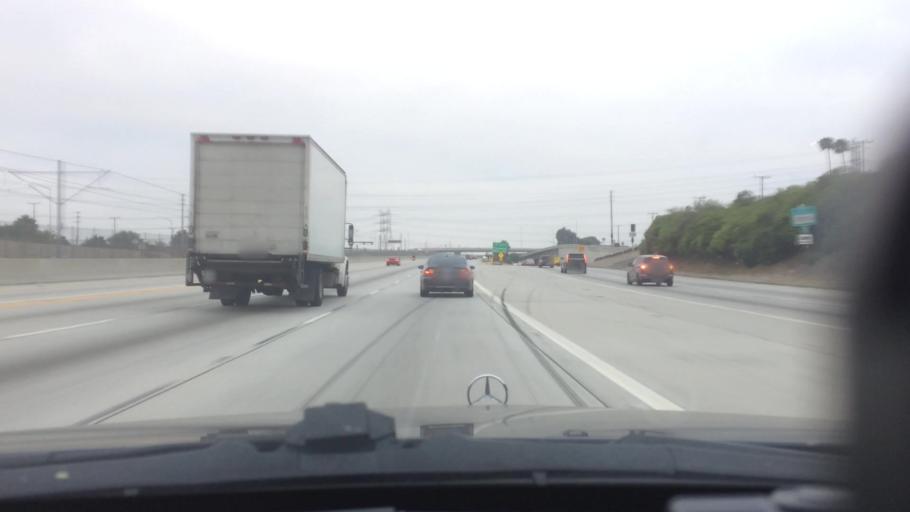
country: US
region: California
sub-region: Los Angeles County
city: Paramount
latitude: 33.9113
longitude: -118.1699
